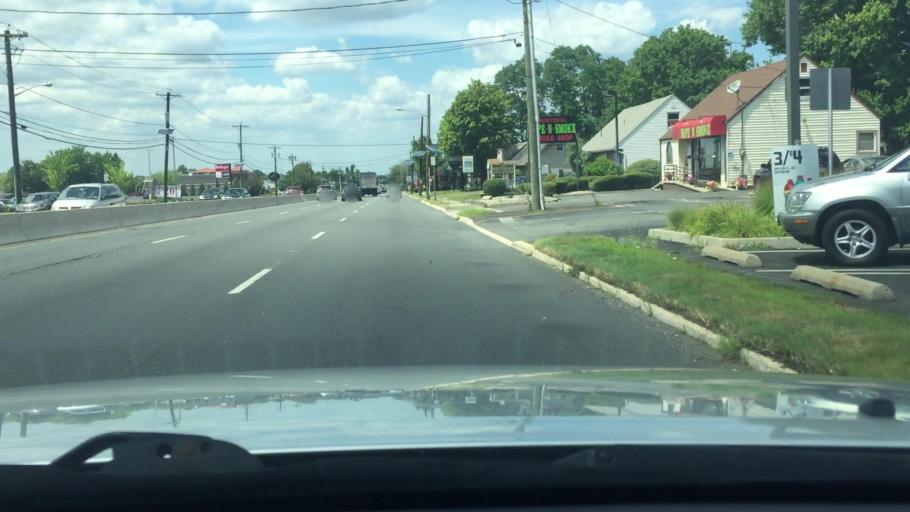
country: US
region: New Jersey
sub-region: Middlesex County
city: South River
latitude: 40.4290
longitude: -74.3837
